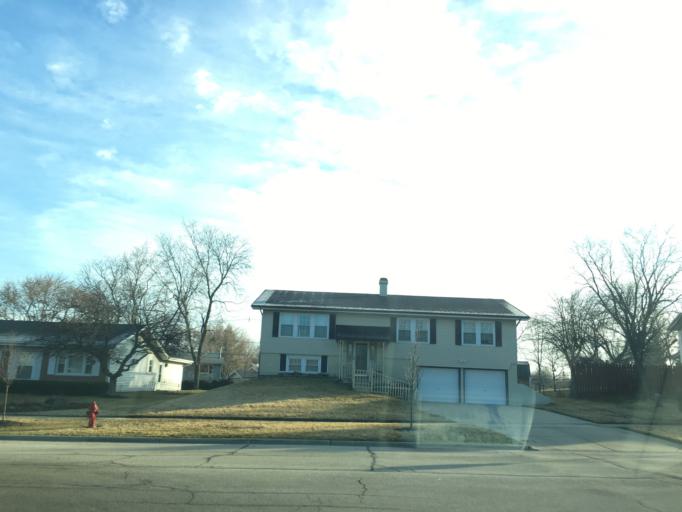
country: US
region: Illinois
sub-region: Cook County
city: Hoffman Estates
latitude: 42.0589
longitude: -88.1058
